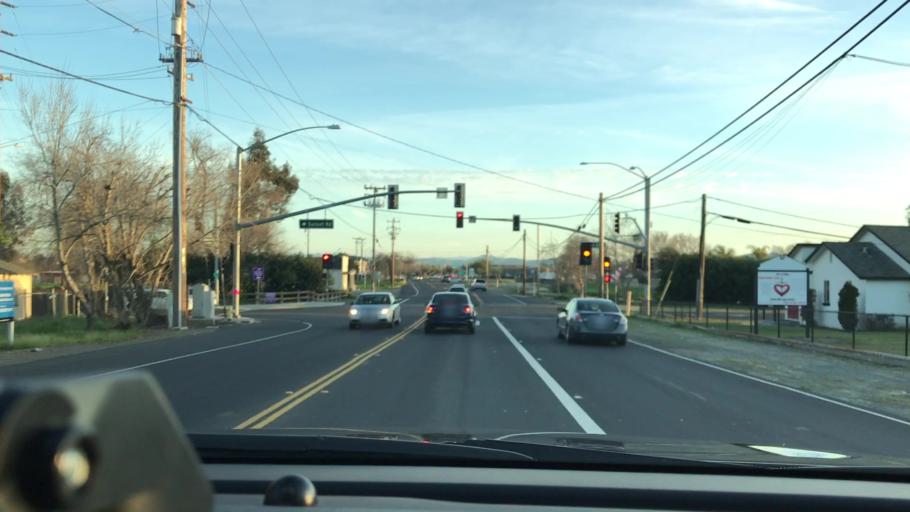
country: US
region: California
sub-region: Contra Costa County
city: Brentwood
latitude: 37.9548
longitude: -121.6962
